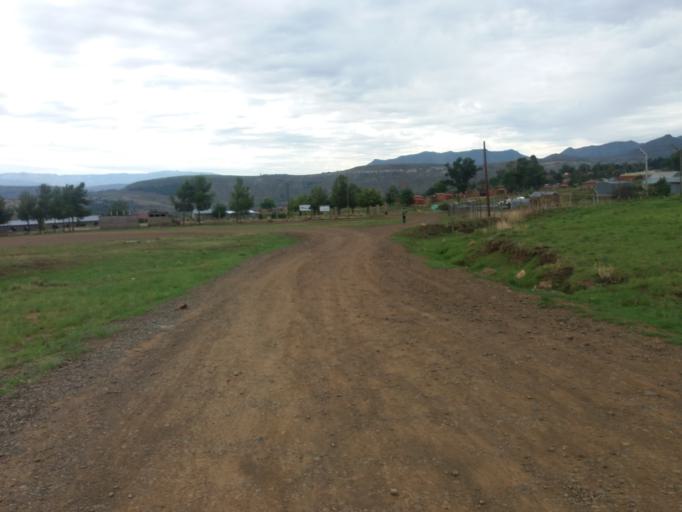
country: LS
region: Quthing
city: Quthing
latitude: -30.4100
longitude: 27.6962
